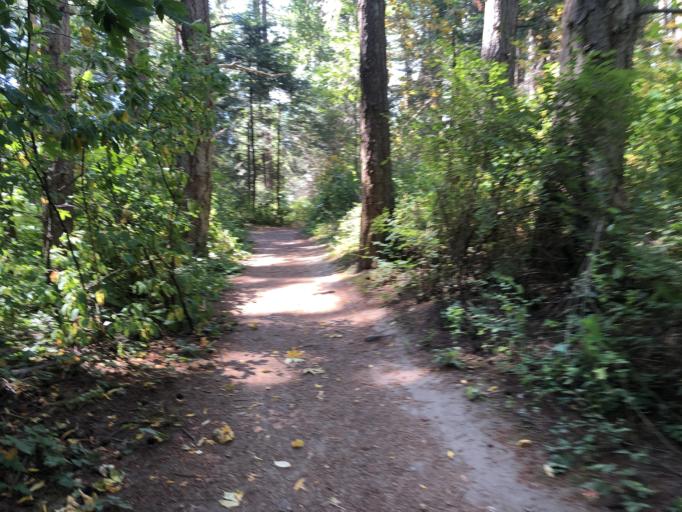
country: CA
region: British Columbia
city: Metchosin
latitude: 48.3651
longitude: -123.5403
